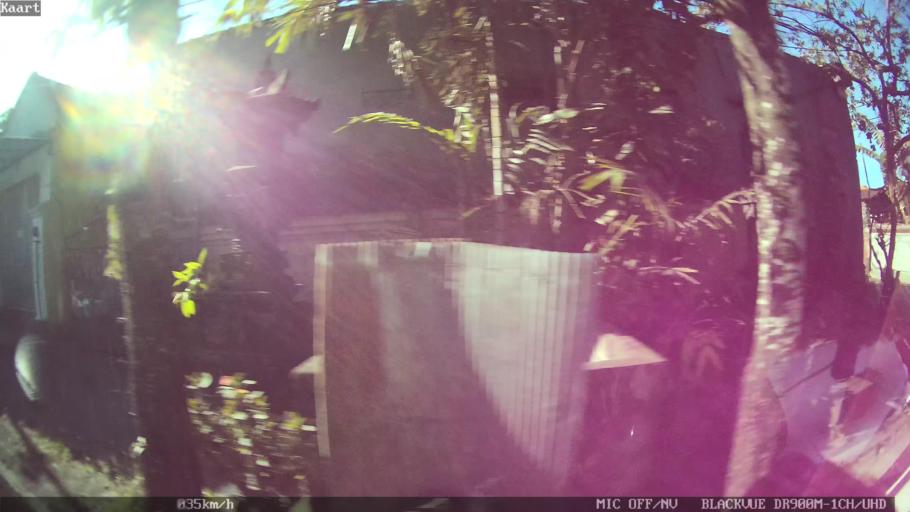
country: ID
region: Bali
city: Banjar Gunungpande
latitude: -8.6441
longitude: 115.1703
